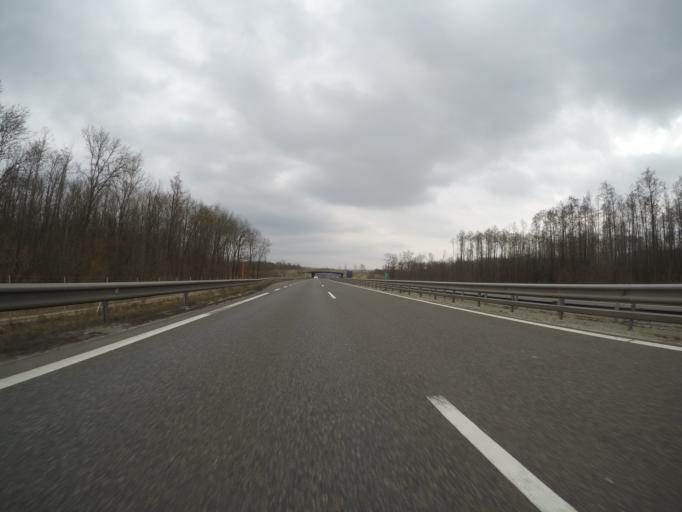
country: SI
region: Lendava-Lendva
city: Lendava
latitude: 46.5948
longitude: 16.4165
